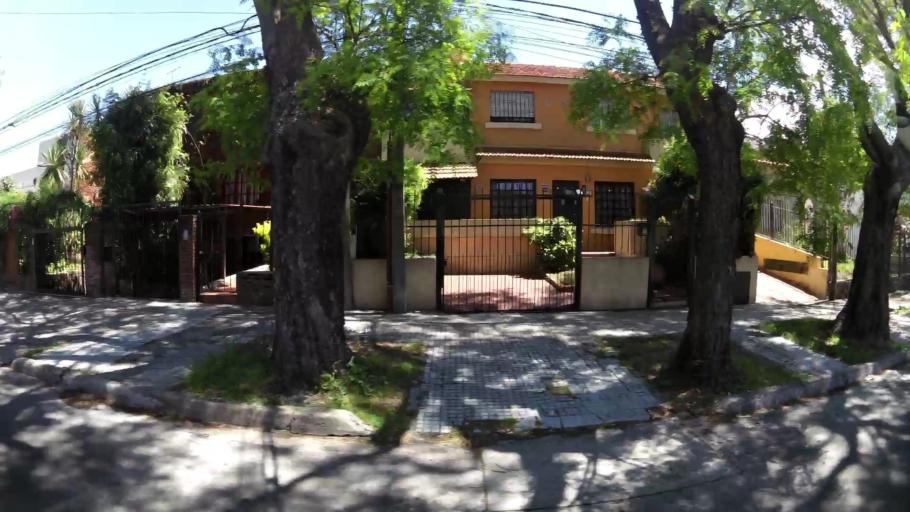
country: UY
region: Montevideo
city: Montevideo
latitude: -34.8914
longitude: -56.1272
